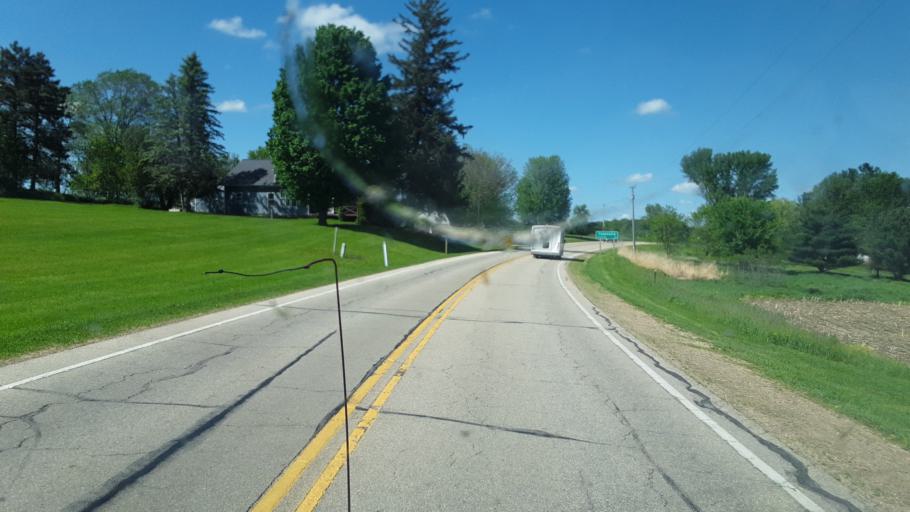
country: US
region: Wisconsin
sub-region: Vernon County
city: Hillsboro
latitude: 43.5165
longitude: -90.2064
